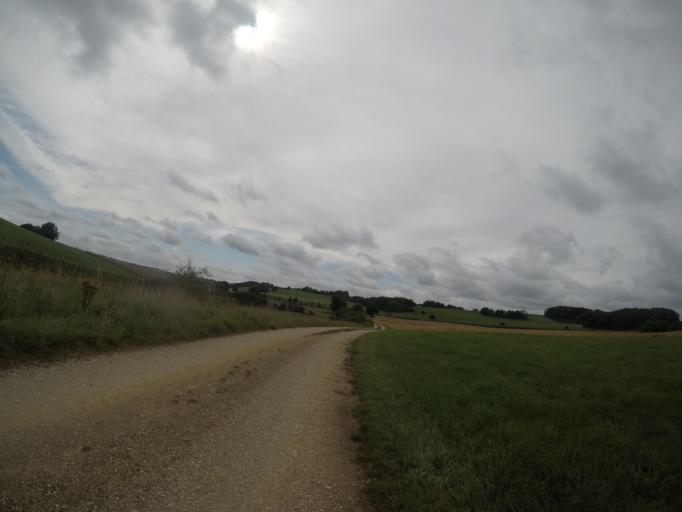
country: DE
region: Baden-Wuerttemberg
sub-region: Tuebingen Region
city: Laichingen
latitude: 48.4616
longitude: 9.6492
